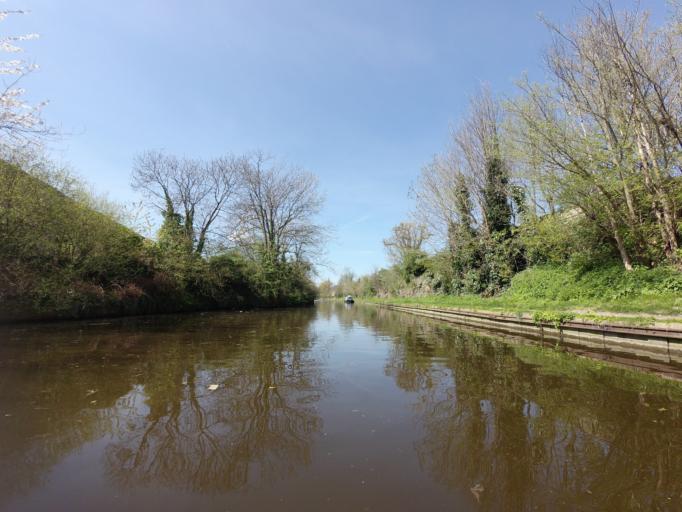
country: GB
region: England
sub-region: Greater London
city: Hayes
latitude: 51.5055
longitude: -0.4215
